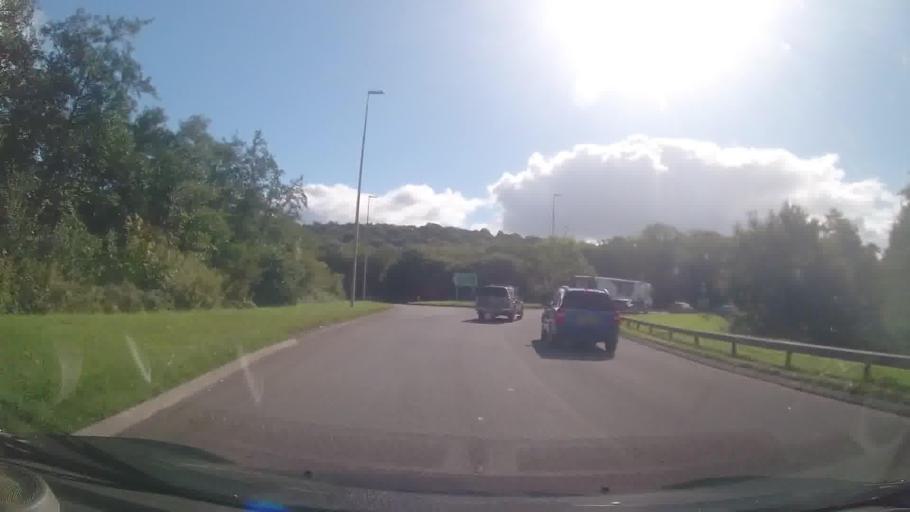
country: GB
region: Wales
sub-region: City and County of Swansea
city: Pontarddulais
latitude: 51.7525
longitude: -4.0639
